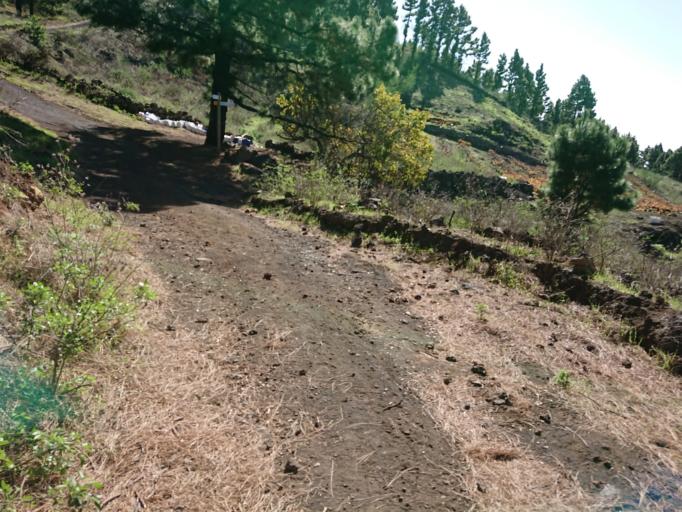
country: ES
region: Canary Islands
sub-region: Provincia de Santa Cruz de Tenerife
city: El Paso
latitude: 28.6063
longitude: -17.8665
